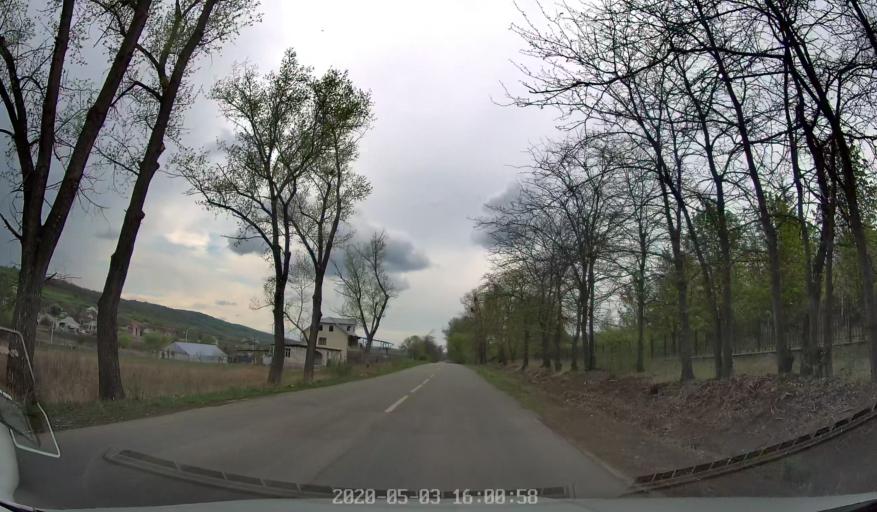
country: MD
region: Stinga Nistrului
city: Bucovat
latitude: 47.1626
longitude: 28.4142
